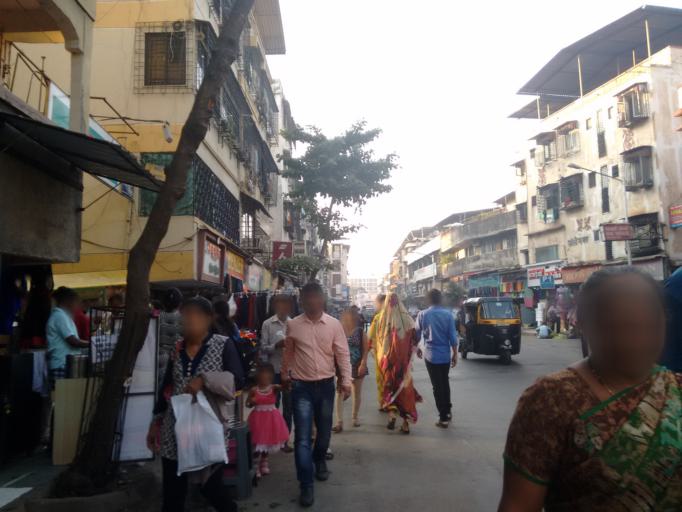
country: IN
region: Maharashtra
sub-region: Thane
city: Bhayandar
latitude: 19.3083
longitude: 72.8546
